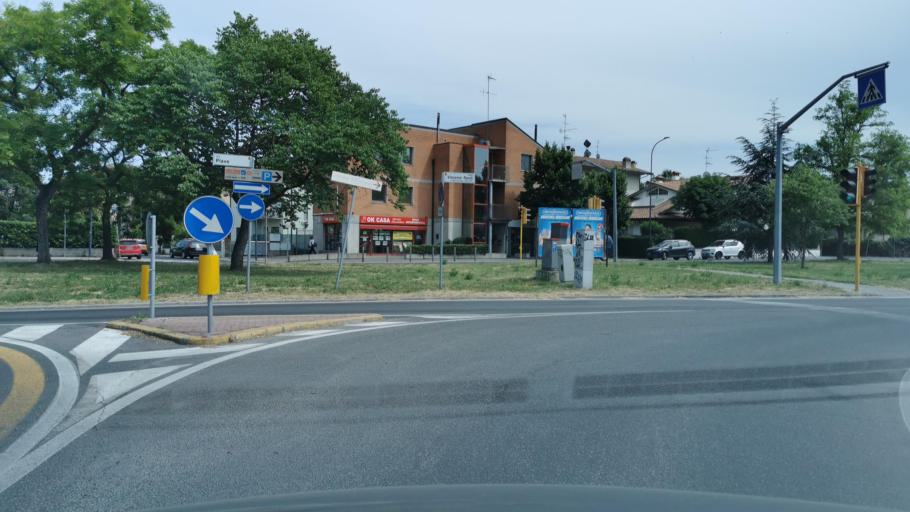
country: IT
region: Emilia-Romagna
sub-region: Provincia di Ravenna
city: Ravenna
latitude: 44.4111
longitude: 12.1924
